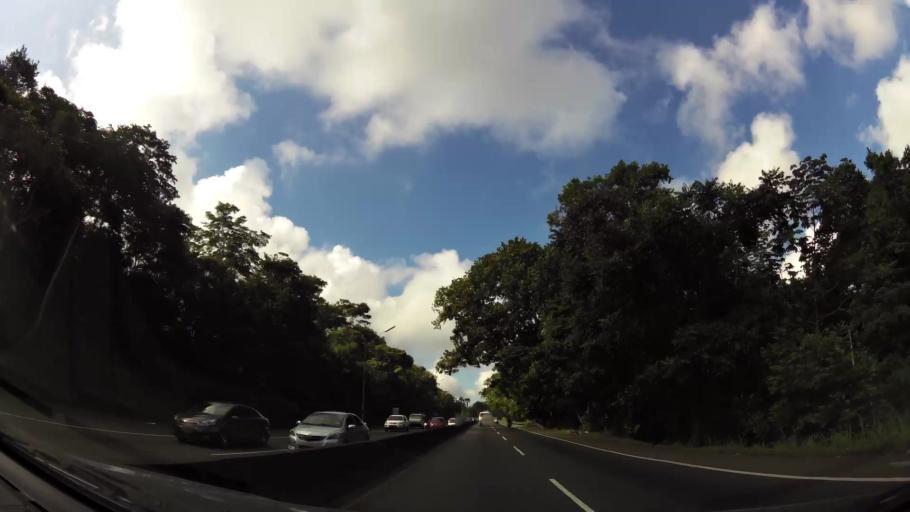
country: PA
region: Panama
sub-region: Distrito Arraijan
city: Arraijan
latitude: 8.9575
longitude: -79.6090
